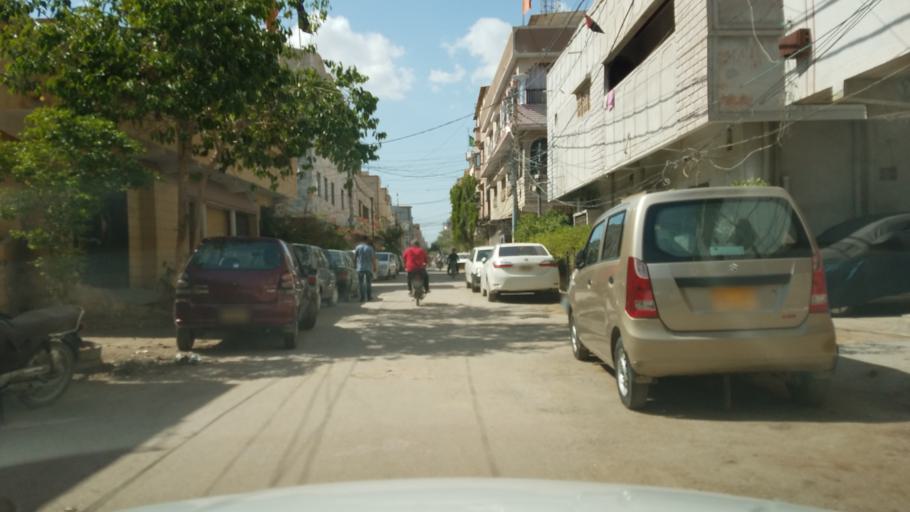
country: PK
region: Sindh
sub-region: Karachi District
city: Karachi
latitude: 24.9470
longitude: 67.0813
